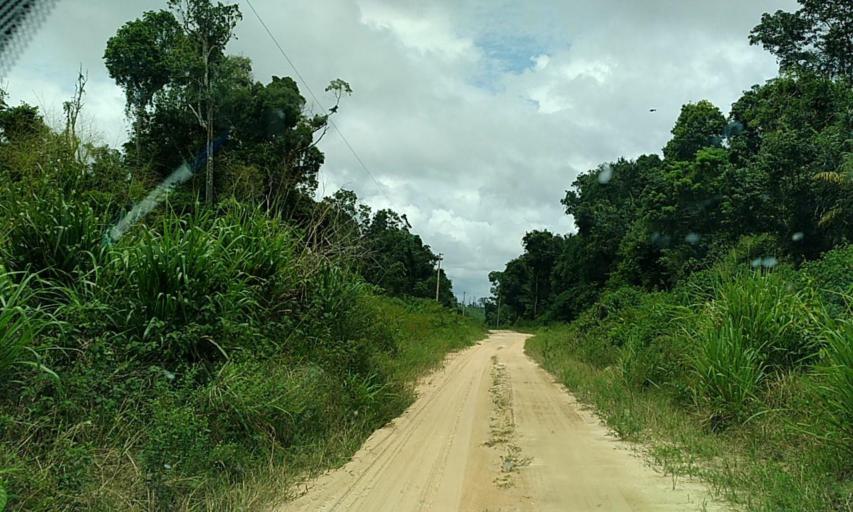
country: BR
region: Para
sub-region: Altamira
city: Altamira
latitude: -3.0702
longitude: -52.9044
